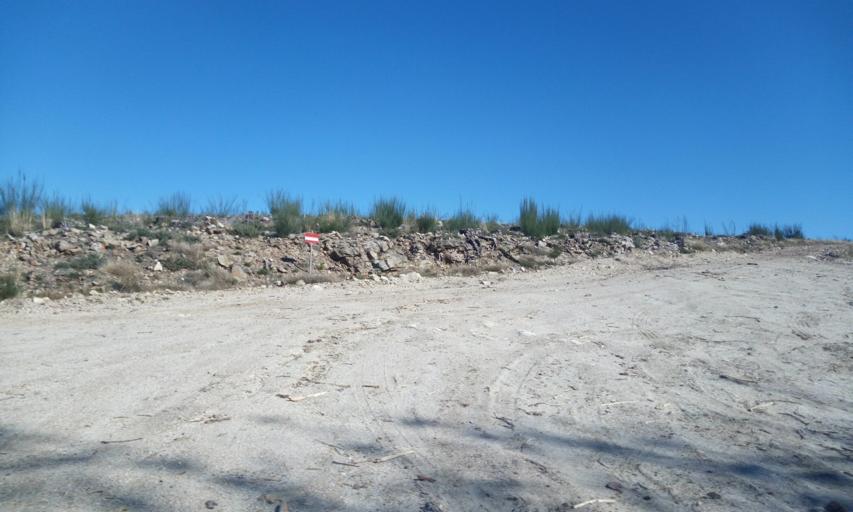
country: PT
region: Guarda
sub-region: Manteigas
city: Manteigas
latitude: 40.4952
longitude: -7.5335
